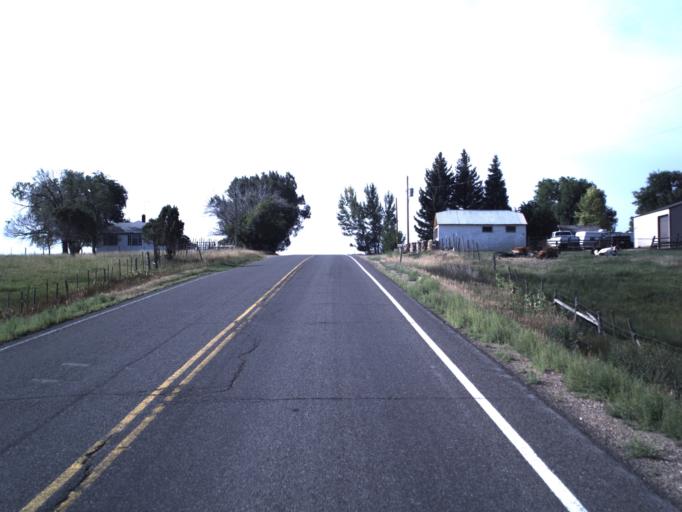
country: US
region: Utah
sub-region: Duchesne County
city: Duchesne
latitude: 40.3320
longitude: -110.4080
